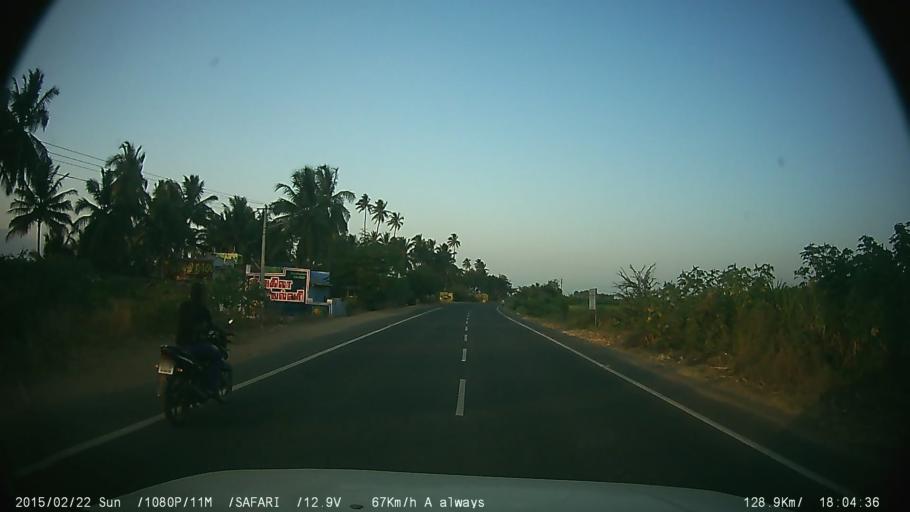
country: IN
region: Tamil Nadu
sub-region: Theni
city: Uttamapalaiyam
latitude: 9.8170
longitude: 77.3508
